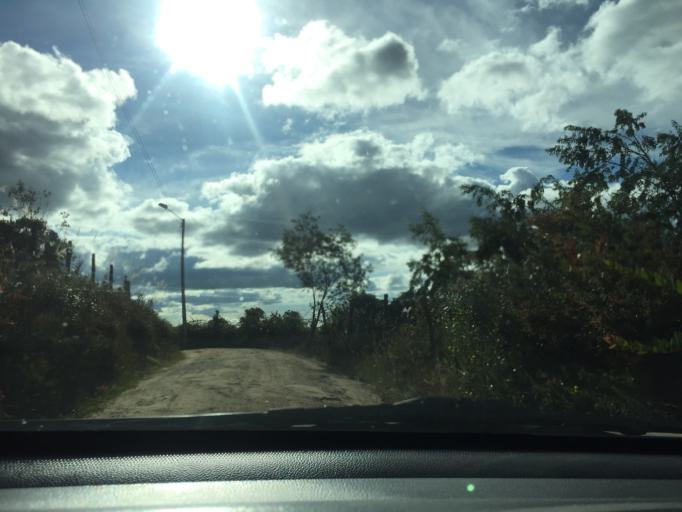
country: CO
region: Cundinamarca
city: Sopo
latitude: 4.9196
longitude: -73.9151
